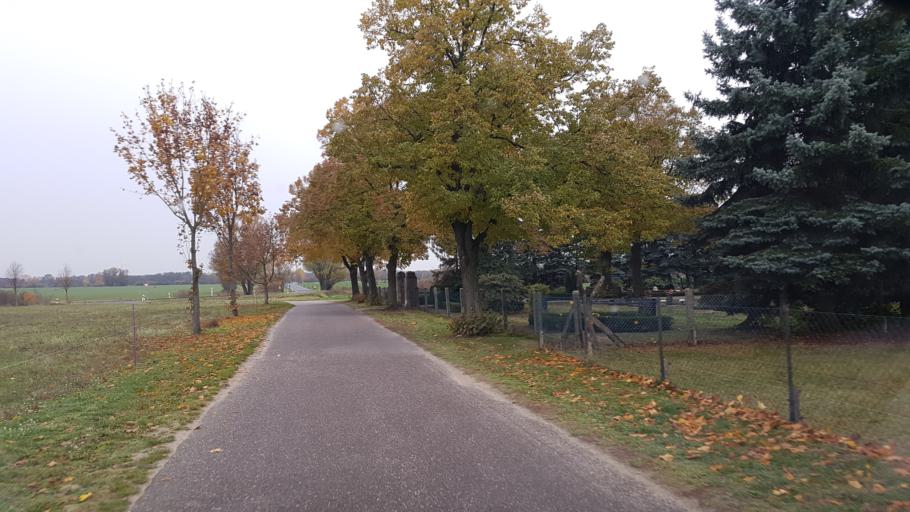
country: DE
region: Brandenburg
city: Finsterwalde
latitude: 51.6847
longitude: 13.7222
